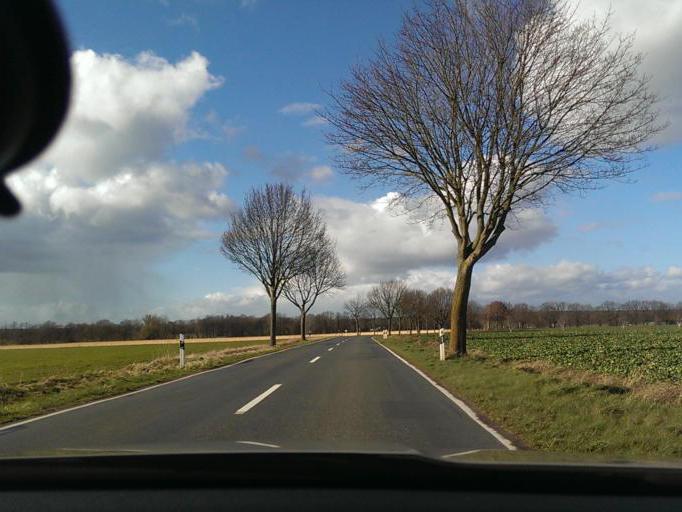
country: DE
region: Lower Saxony
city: Elze
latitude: 52.5397
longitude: 9.6841
